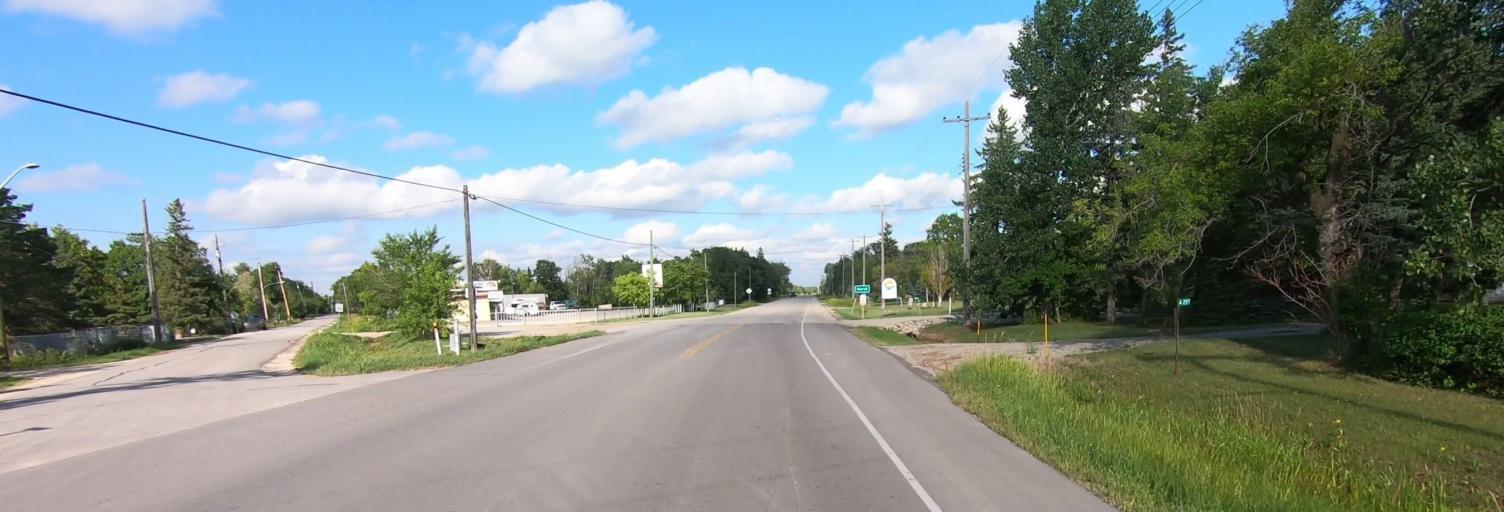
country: CA
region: Manitoba
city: Selkirk
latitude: 50.0259
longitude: -97.0256
